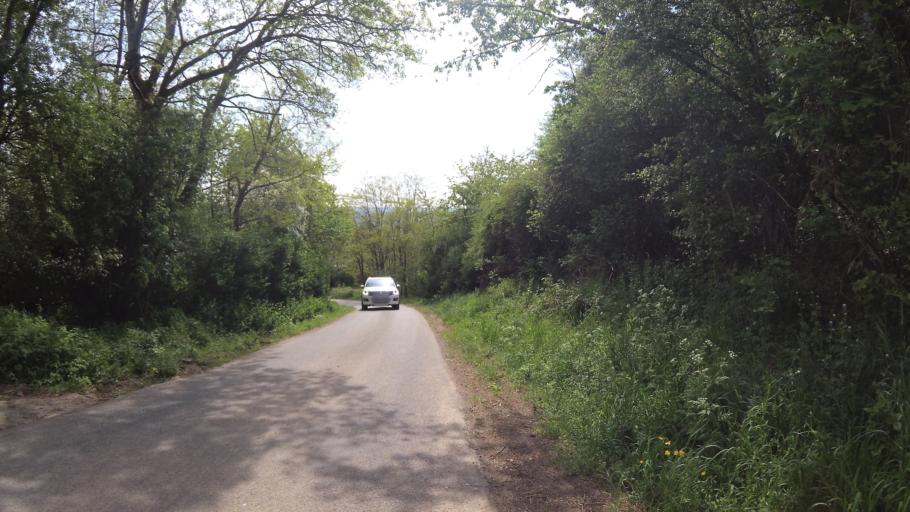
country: DE
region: Saarland
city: Hangard
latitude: 49.3815
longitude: 7.1926
